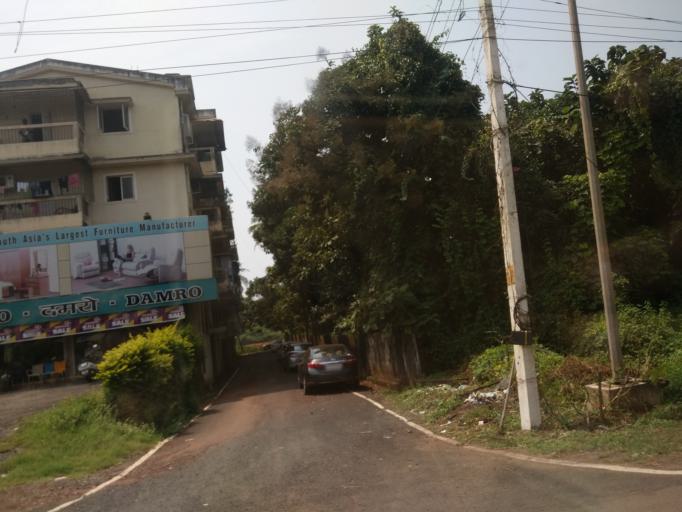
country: IN
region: Goa
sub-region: South Goa
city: Raia
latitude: 15.3181
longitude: 73.9421
